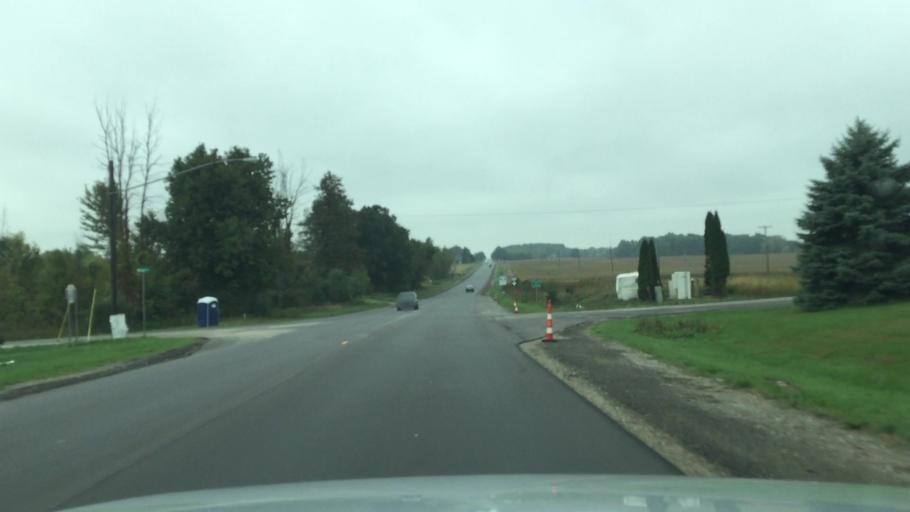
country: US
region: Michigan
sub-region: Shiawassee County
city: Perry
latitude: 42.8639
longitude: -84.2210
